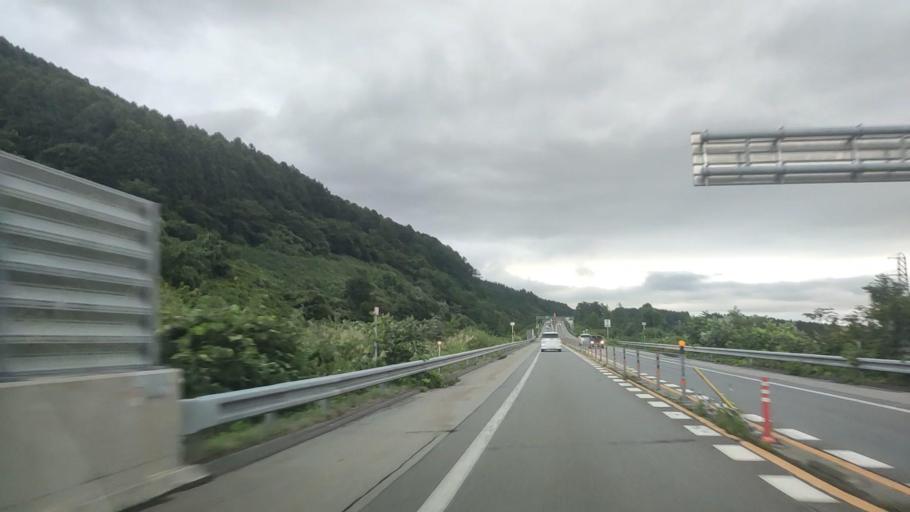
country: JP
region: Hokkaido
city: Nanae
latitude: 41.9132
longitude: 140.6912
